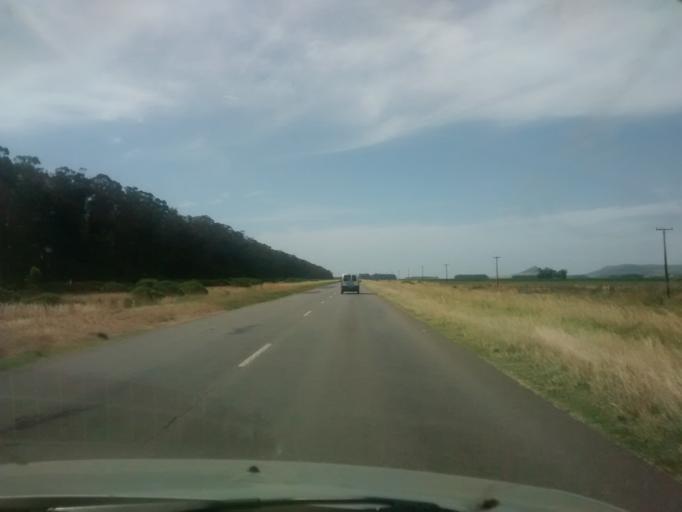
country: AR
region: Buenos Aires
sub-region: Partido de Loberia
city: Loberia
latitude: -37.9400
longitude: -58.6906
